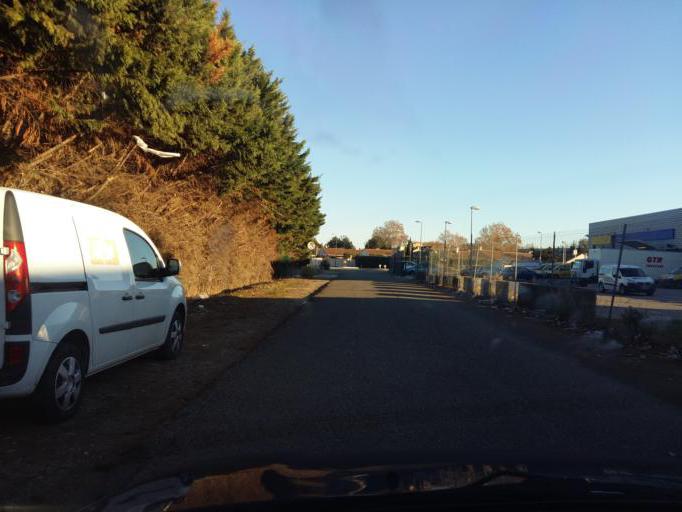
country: FR
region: Provence-Alpes-Cote d'Azur
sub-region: Departement du Vaucluse
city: Le Pontet
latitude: 43.9347
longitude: 4.8397
